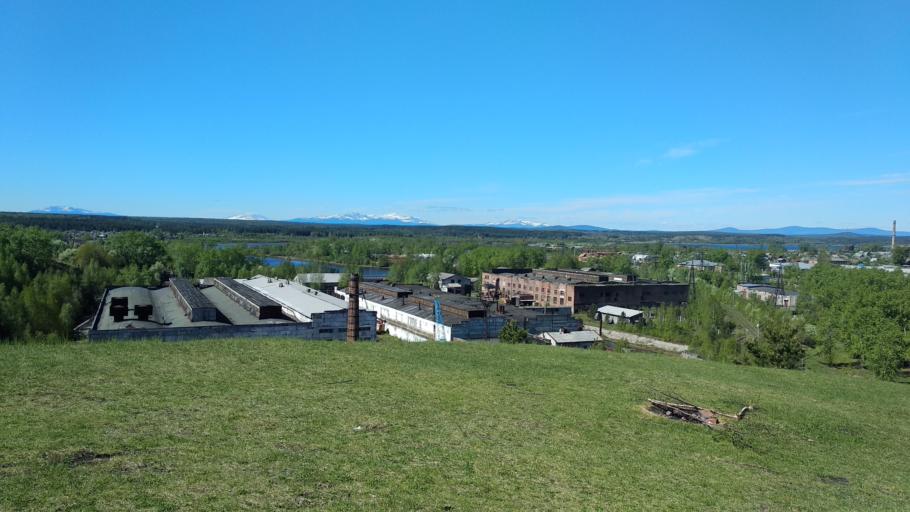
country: RU
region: Sverdlovsk
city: Karpinsk
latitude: 59.7498
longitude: 60.0157
